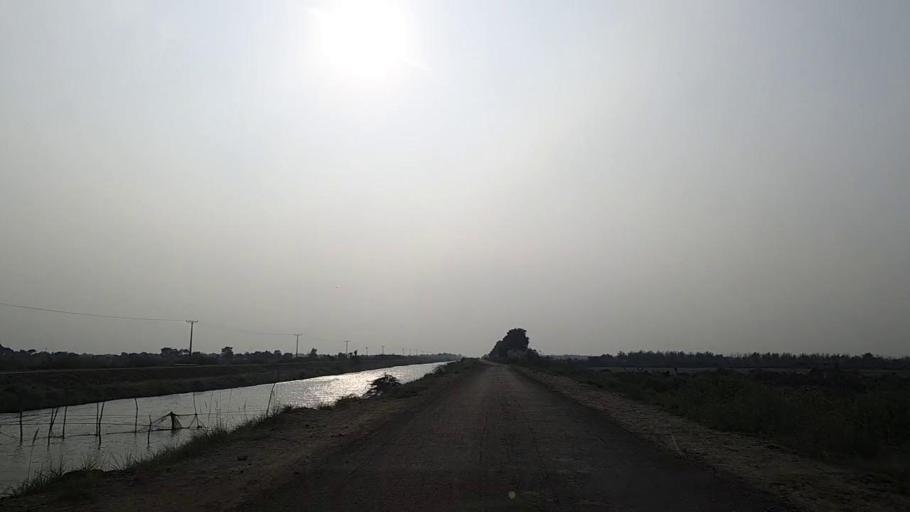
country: PK
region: Sindh
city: Mirpur Sakro
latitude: 24.6324
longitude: 67.5800
